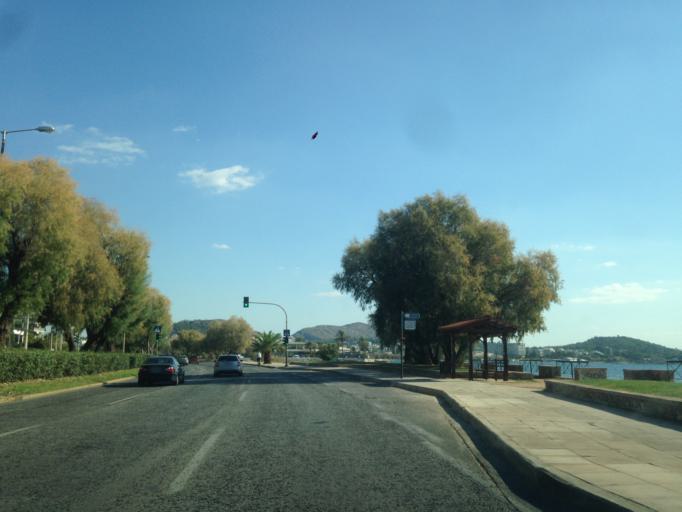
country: GR
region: Attica
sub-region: Nomarchia Anatolikis Attikis
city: Voula
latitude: 37.8377
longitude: 23.7638
